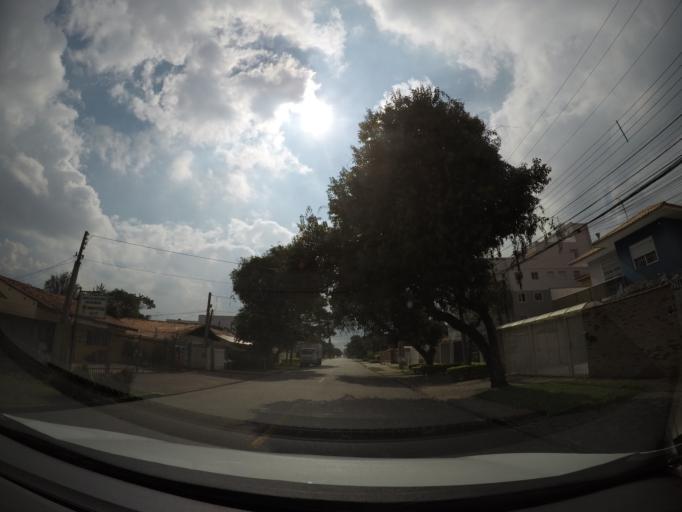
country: BR
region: Parana
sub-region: Sao Jose Dos Pinhais
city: Sao Jose dos Pinhais
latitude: -25.4891
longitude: -49.2476
